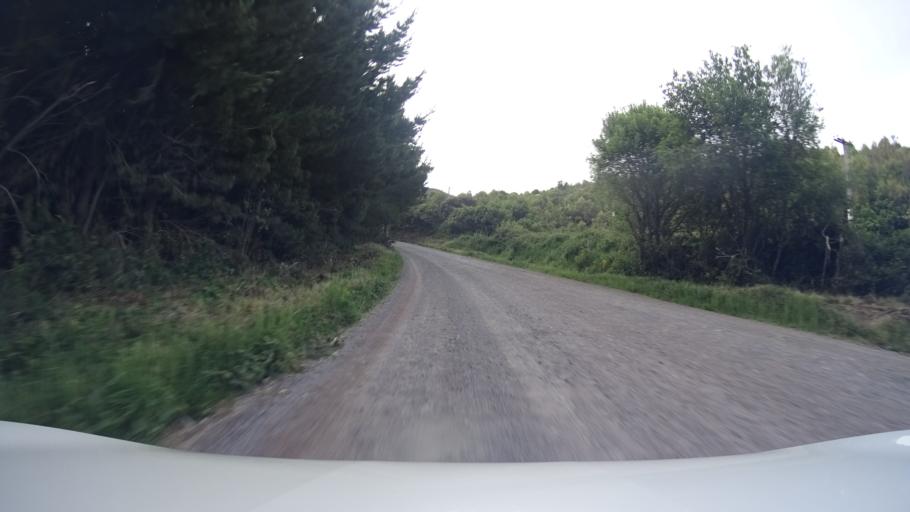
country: NZ
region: Bay of Plenty
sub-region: Rotorua District
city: Rotorua
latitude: -38.3301
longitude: 176.3792
